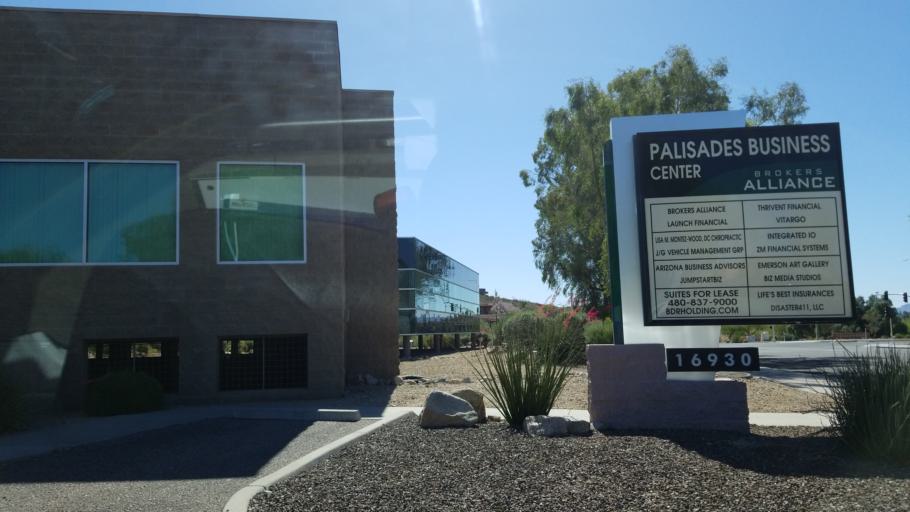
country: US
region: Arizona
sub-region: Maricopa County
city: Fountain Hills
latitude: 33.6071
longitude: -111.7150
